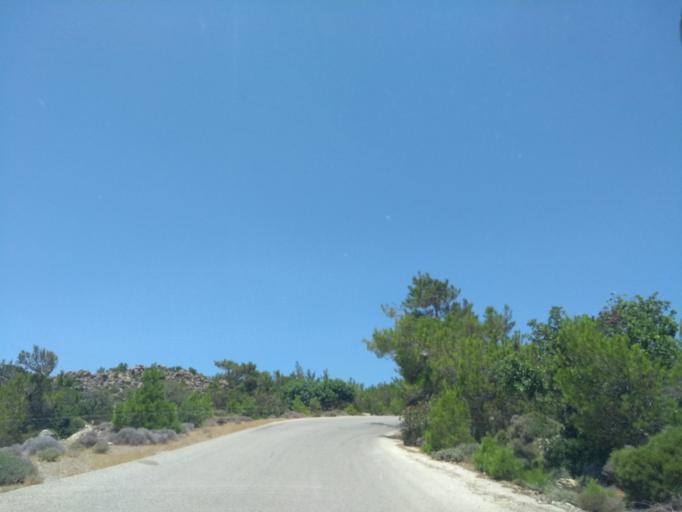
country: GR
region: Crete
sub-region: Nomos Chanias
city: Vryses
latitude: 35.3310
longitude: 23.5438
